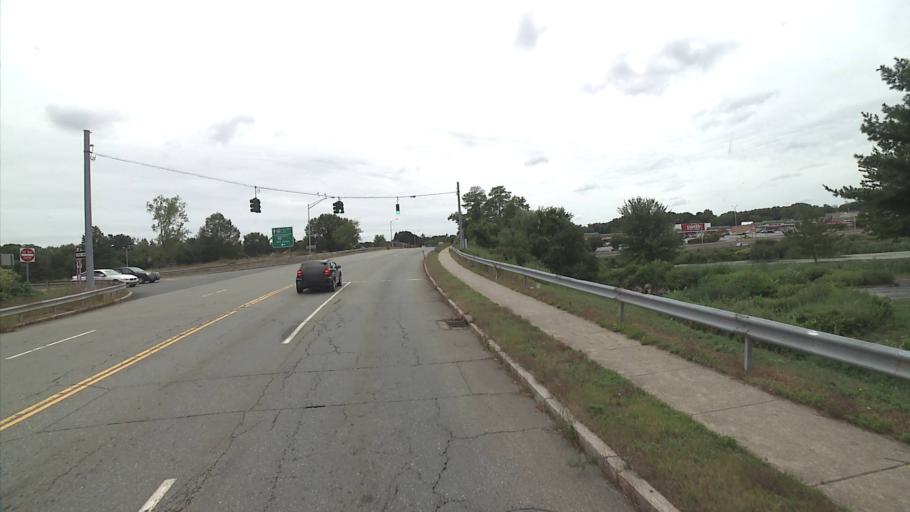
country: US
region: Connecticut
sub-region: New London County
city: New London
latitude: 41.3701
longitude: -72.1148
